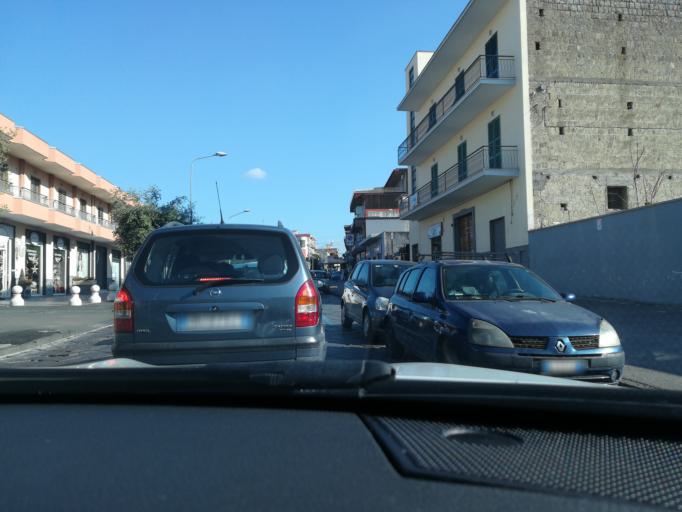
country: IT
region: Campania
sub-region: Provincia di Napoli
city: Sant'Anastasia
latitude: 40.8702
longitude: 14.3935
